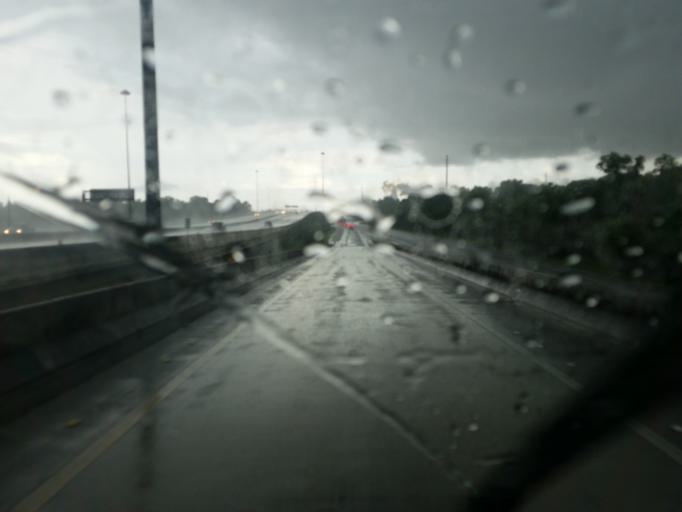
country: US
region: Alabama
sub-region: Mobile County
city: Prichard
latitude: 30.7311
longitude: -88.0771
